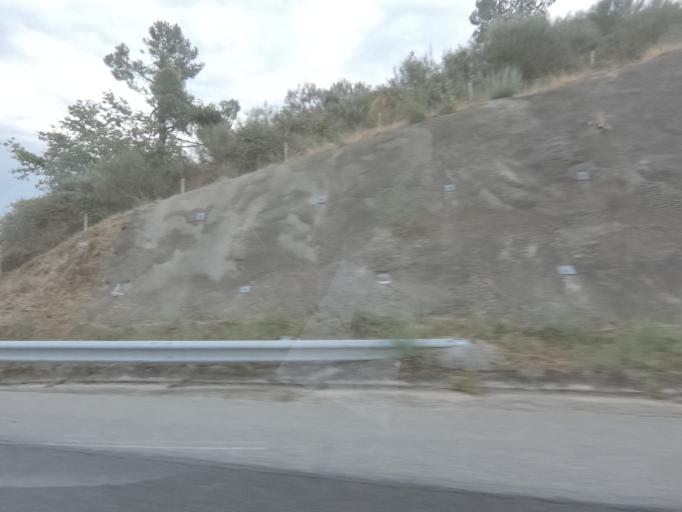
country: PT
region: Viseu
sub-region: Lamego
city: Lamego
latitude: 41.0687
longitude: -7.8302
